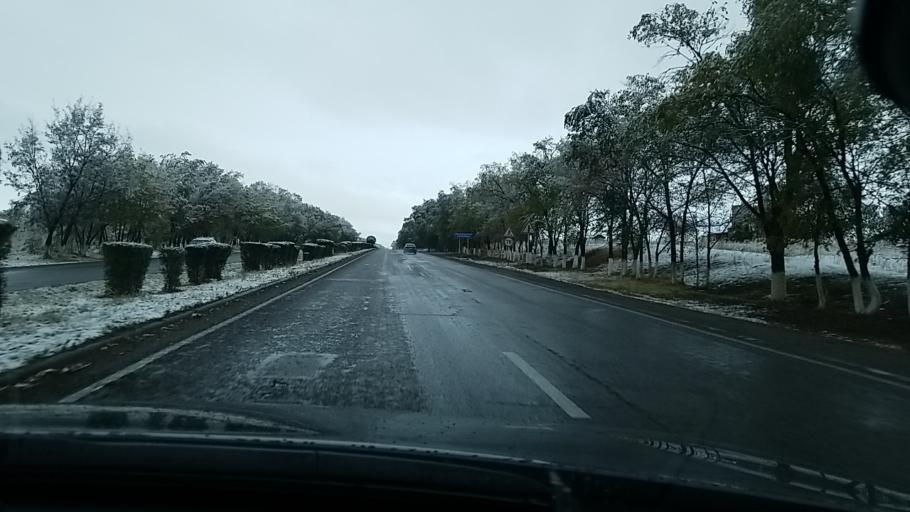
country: KZ
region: Almaty Oblysy
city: Burunday
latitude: 43.2203
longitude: 76.4678
